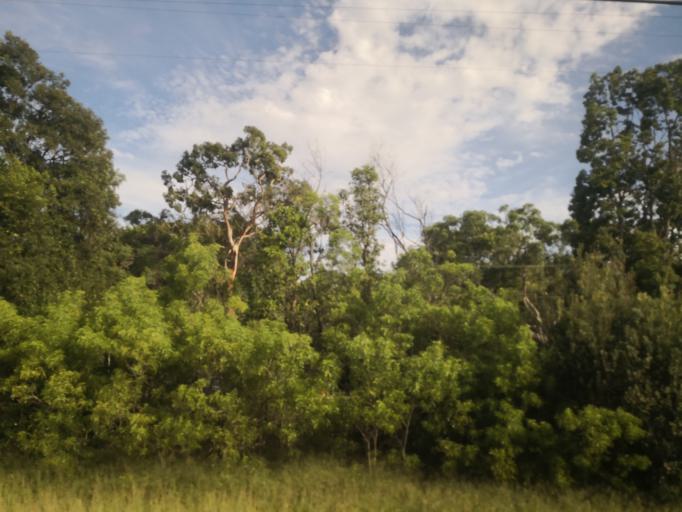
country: AU
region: New South Wales
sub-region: Gosford Shire
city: Blackwall
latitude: -33.4967
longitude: 151.3078
